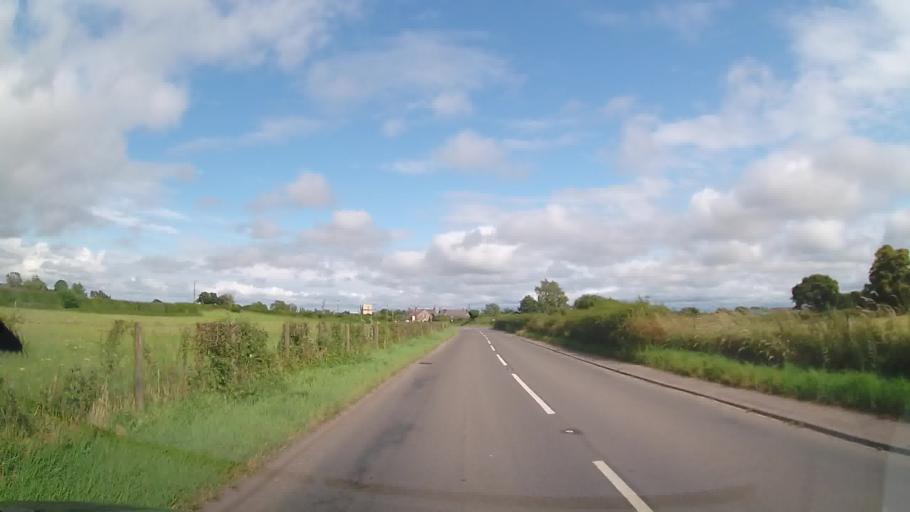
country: GB
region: England
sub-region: Shropshire
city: Pant
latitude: 52.8099
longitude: -3.0578
